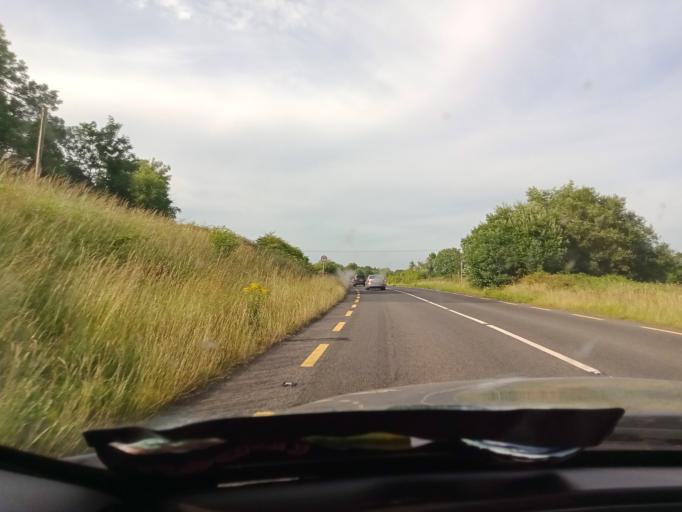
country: IE
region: Ulster
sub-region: An Cabhan
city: Cavan
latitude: 53.9104
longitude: -7.4371
